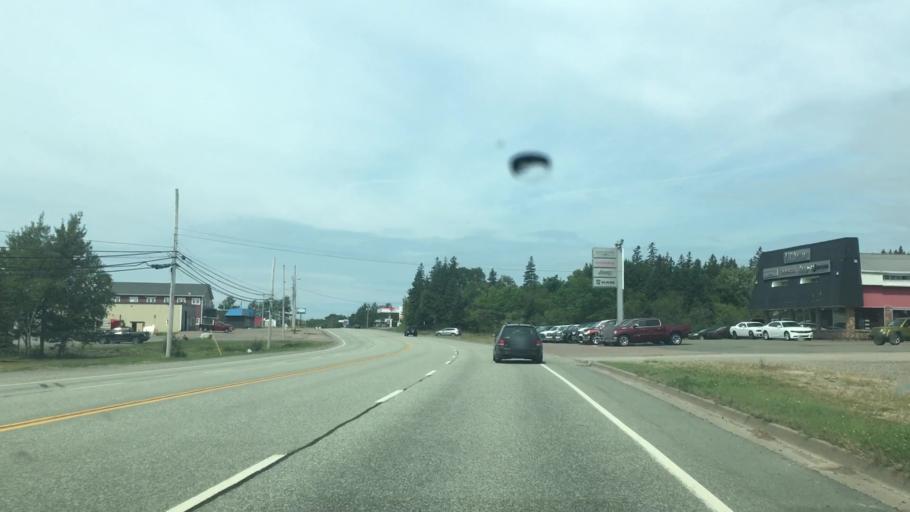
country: CA
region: Nova Scotia
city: Port Hawkesbury
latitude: 45.6390
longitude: -61.3844
